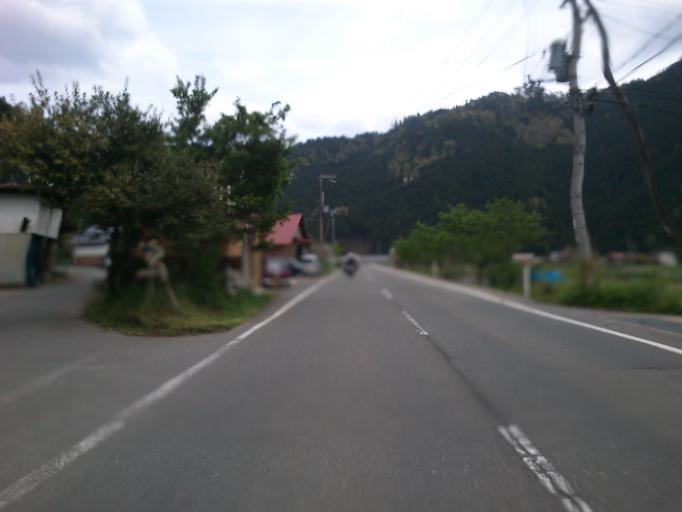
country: JP
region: Fukui
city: Obama
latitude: 35.3048
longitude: 135.6220
